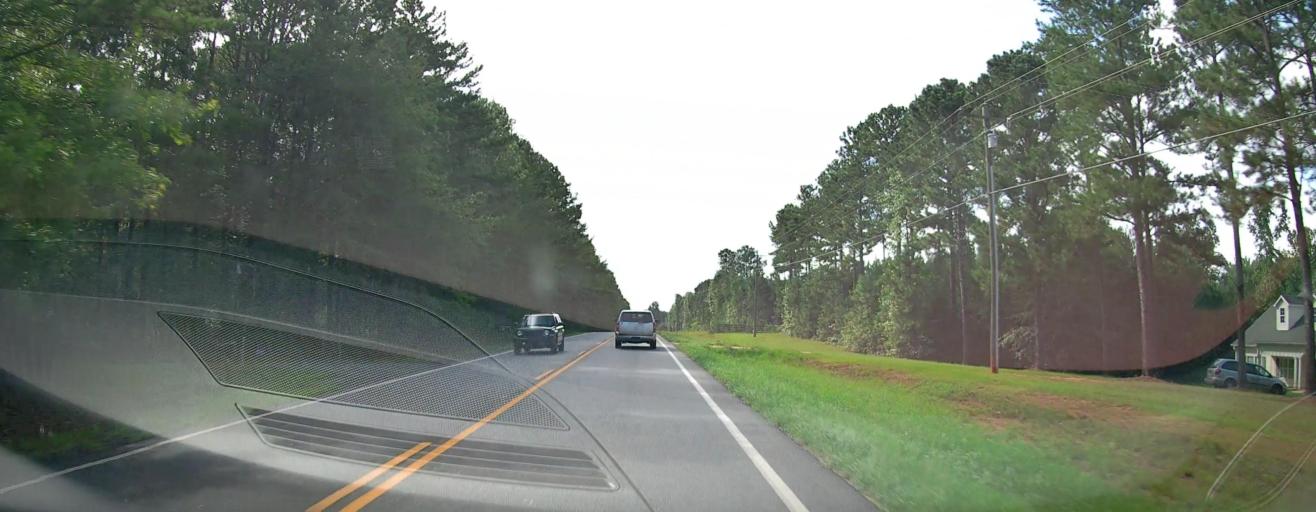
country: US
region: Georgia
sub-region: Upson County
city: Hannahs Mill
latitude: 32.9706
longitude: -84.4836
